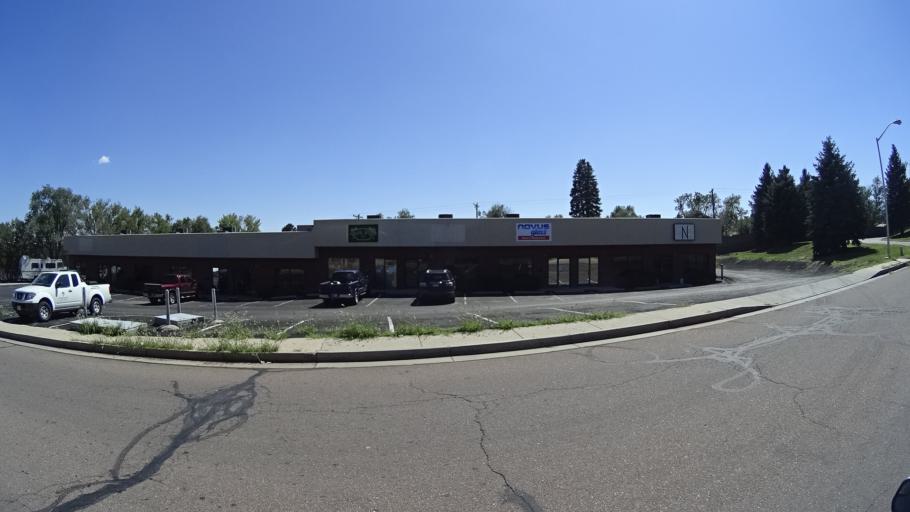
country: US
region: Colorado
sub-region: El Paso County
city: Colorado Springs
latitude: 38.8369
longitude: -104.7682
